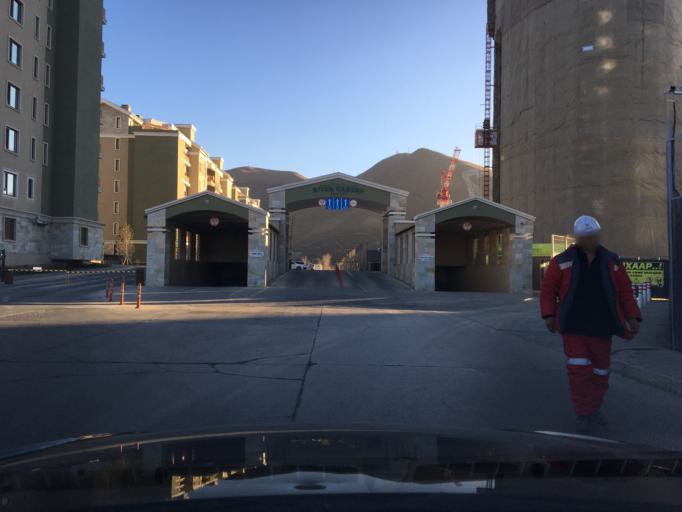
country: MN
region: Ulaanbaatar
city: Ulaanbaatar
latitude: 47.8908
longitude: 106.9284
